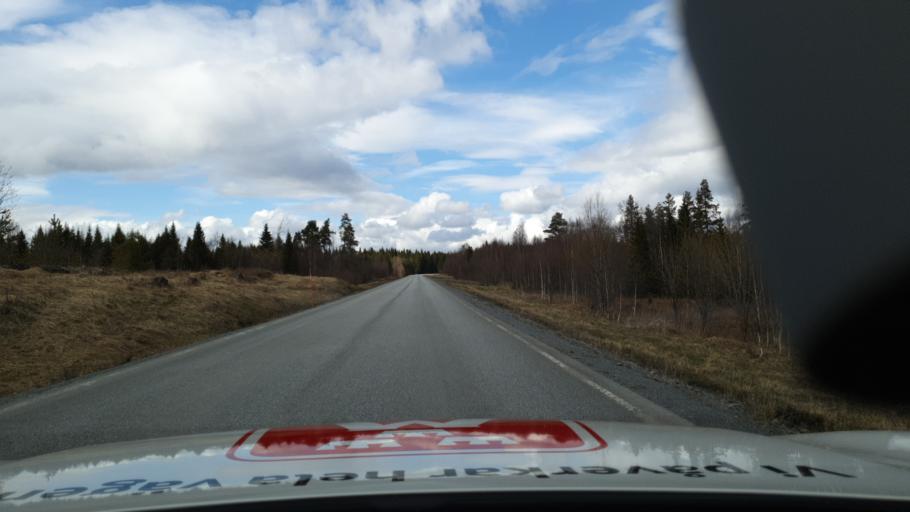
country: SE
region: Jaemtland
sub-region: Krokoms Kommun
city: Krokom
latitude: 63.2963
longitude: 14.4301
